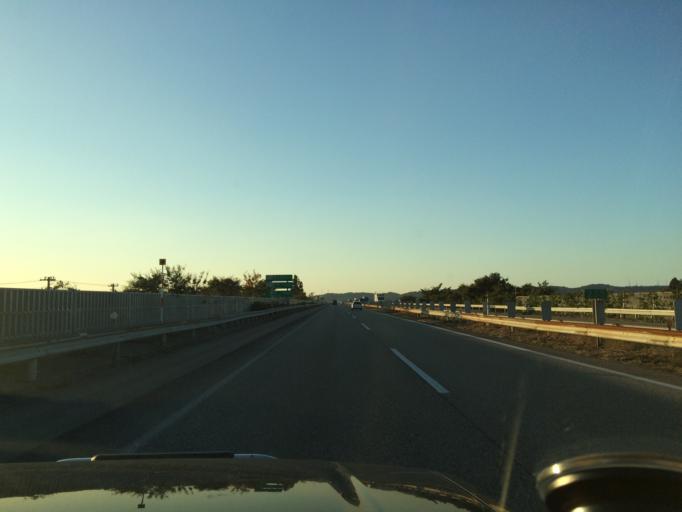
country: JP
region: Toyama
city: Toyama-shi
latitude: 36.6608
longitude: 137.1964
